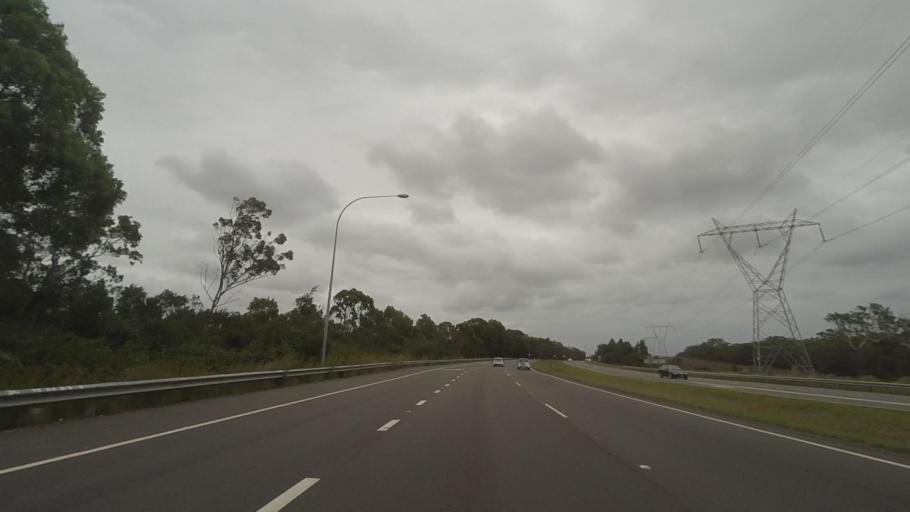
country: AU
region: New South Wales
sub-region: Wyong Shire
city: Buff Point
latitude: -33.2060
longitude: 151.5154
